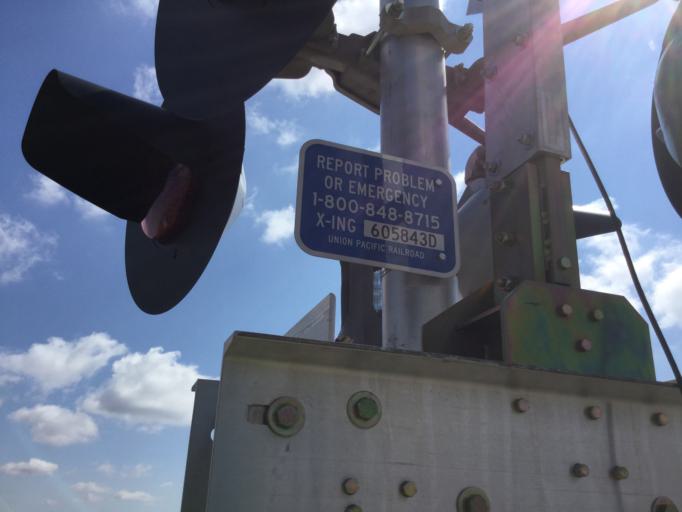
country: US
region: Kansas
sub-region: Kiowa County
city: Greensburg
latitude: 37.5927
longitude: -99.4124
